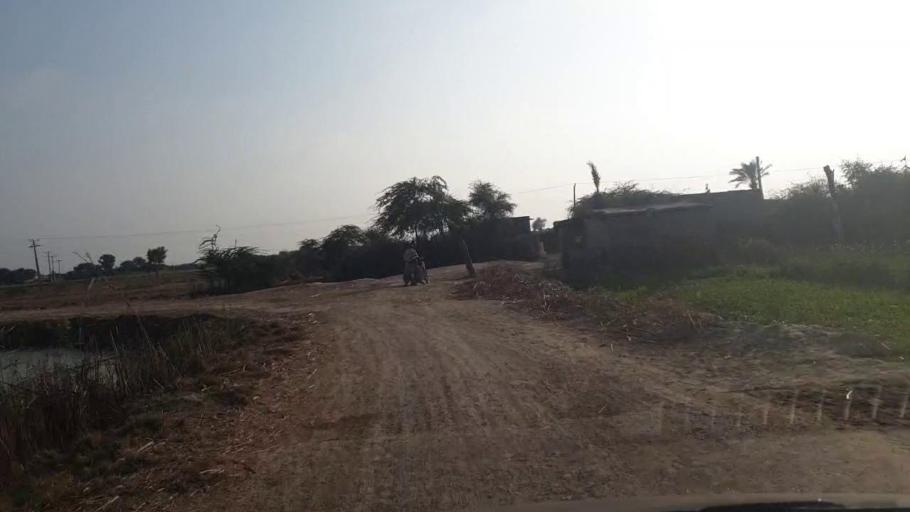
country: PK
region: Sindh
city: Shahdadpur
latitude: 25.8767
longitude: 68.7299
